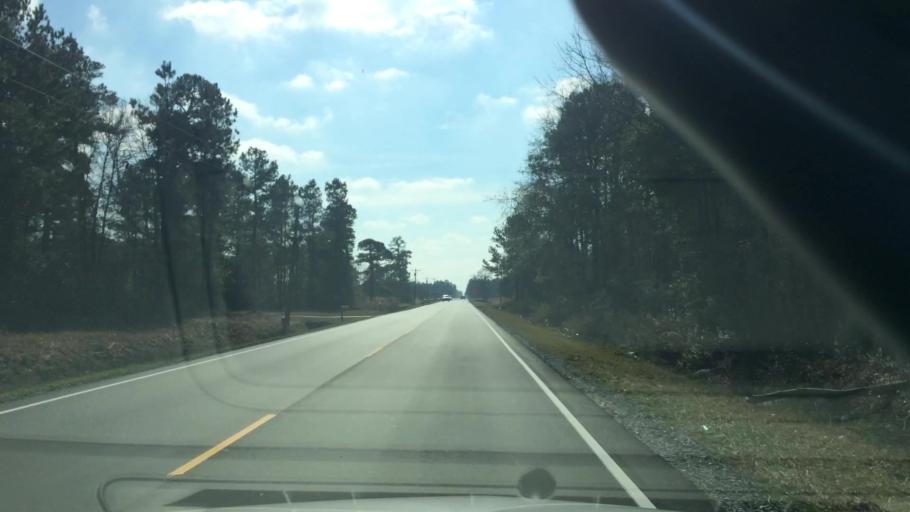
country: US
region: North Carolina
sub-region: Duplin County
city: Beulaville
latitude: 35.0242
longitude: -77.7495
